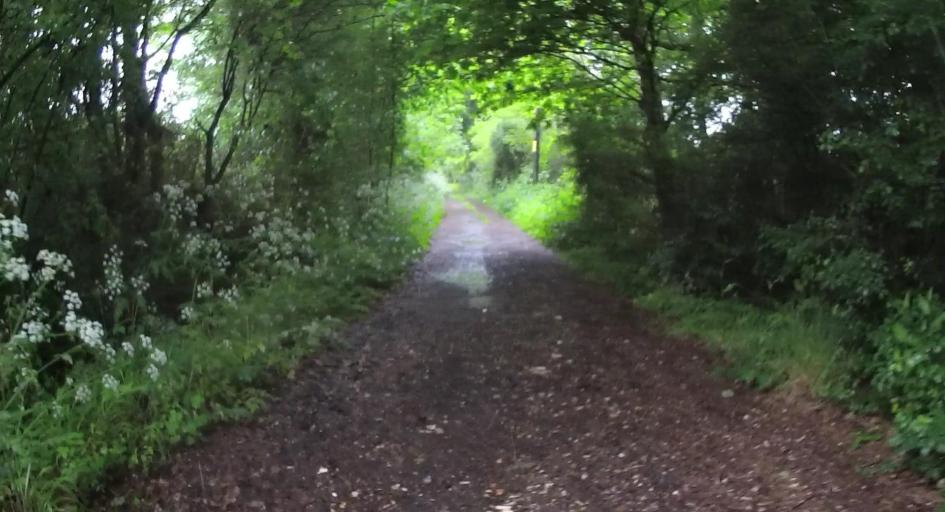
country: GB
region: England
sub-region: Wokingham
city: Wokingham
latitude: 51.3998
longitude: -0.8072
